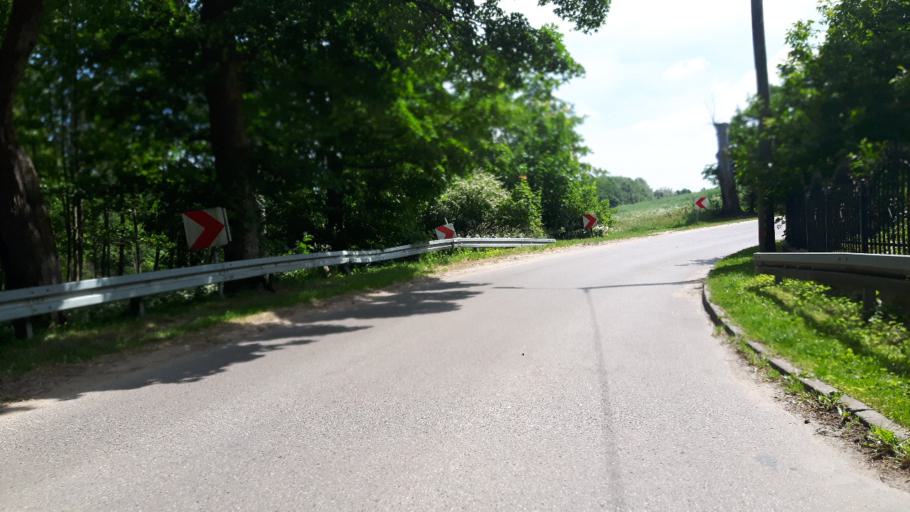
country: PL
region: Pomeranian Voivodeship
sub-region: Powiat wejherowski
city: Choczewo
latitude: 54.7554
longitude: 17.7910
